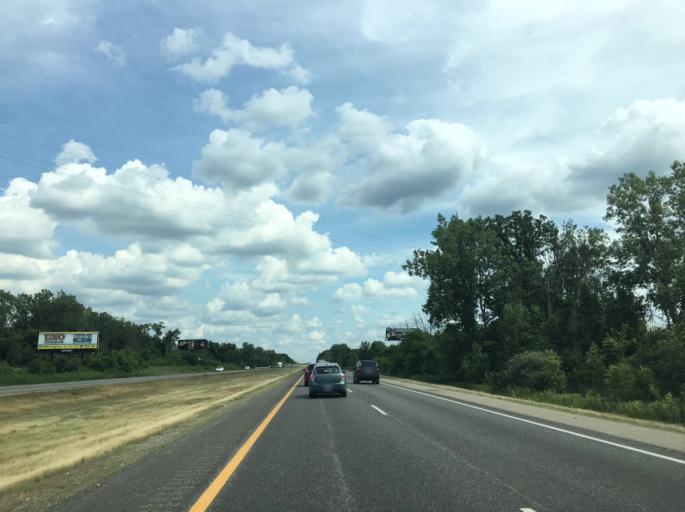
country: US
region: Michigan
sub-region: Genesee County
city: Flint
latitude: 42.9435
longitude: -83.7125
